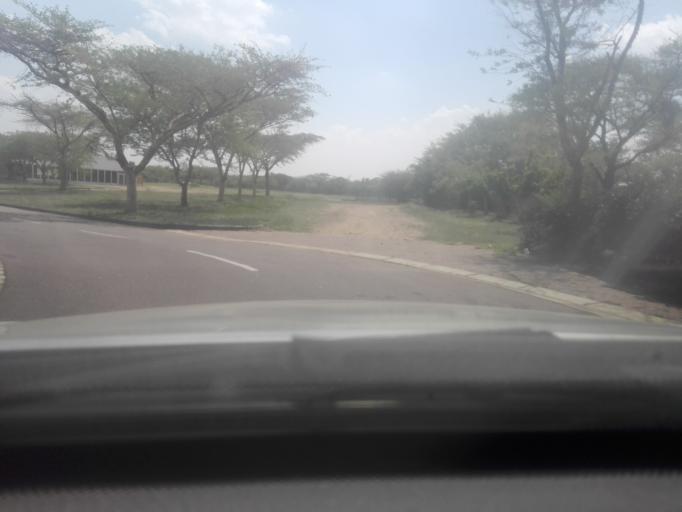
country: BW
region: Kweneng
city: Mogoditshane
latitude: -24.6389
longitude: 25.8768
